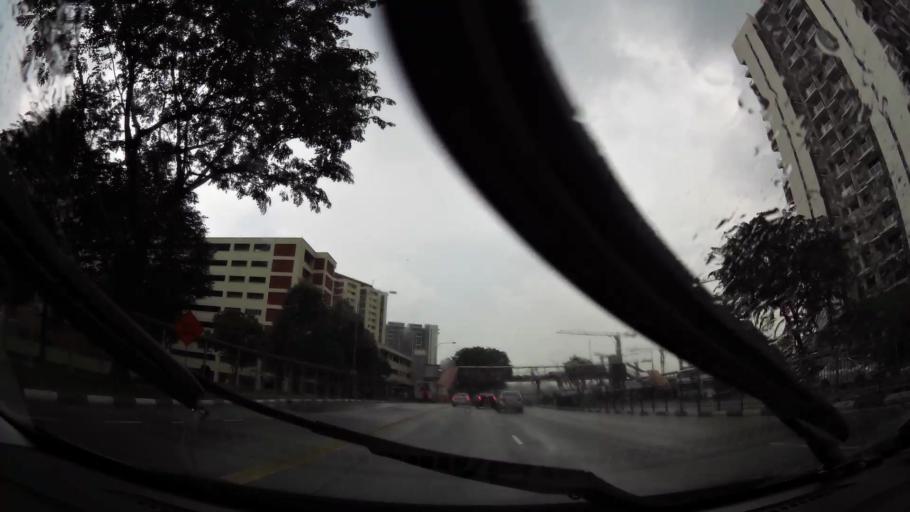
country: SG
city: Singapore
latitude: 1.3330
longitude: 103.8694
